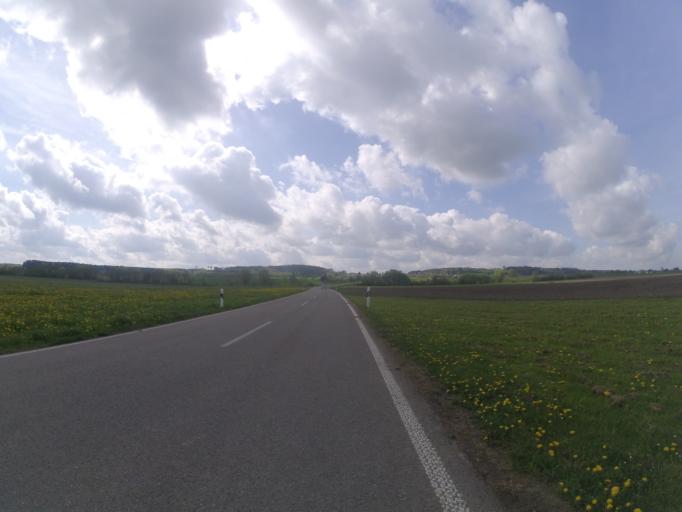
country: DE
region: Baden-Wuerttemberg
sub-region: Tuebingen Region
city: Griesingen
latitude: 48.2388
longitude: 9.7684
